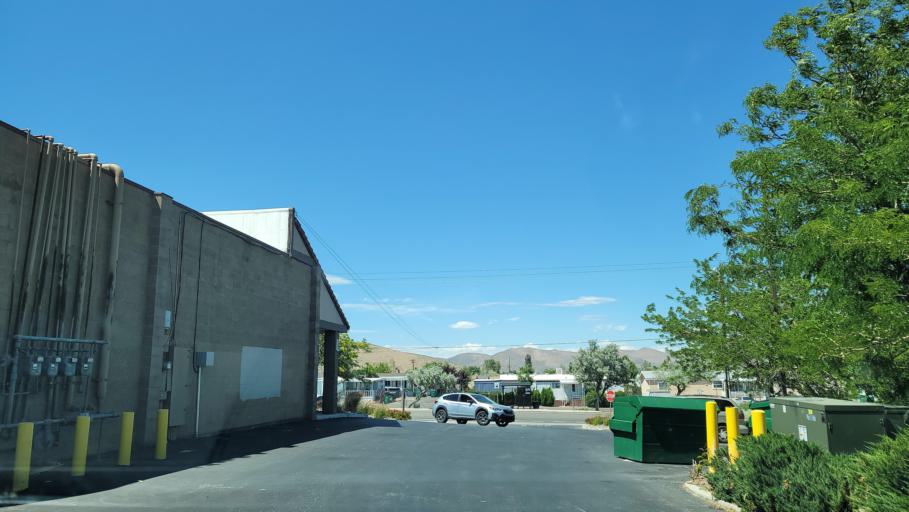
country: US
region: Nevada
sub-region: Carson City
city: Carson City
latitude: 39.1333
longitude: -119.7672
